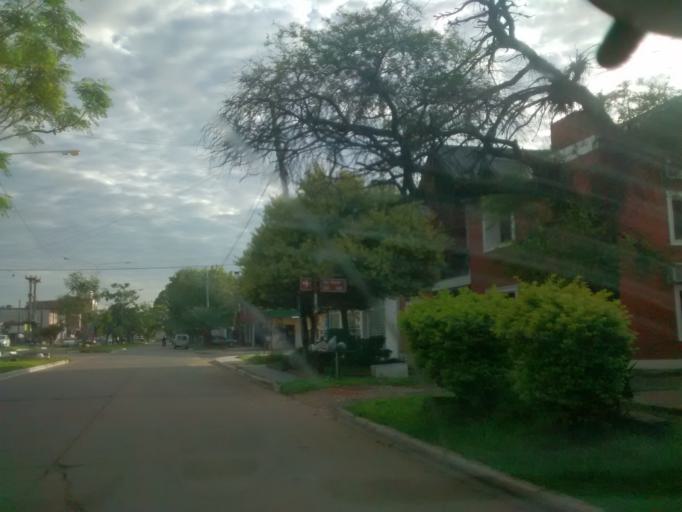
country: AR
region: Chaco
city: Resistencia
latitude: -27.4576
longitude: -59.0023
